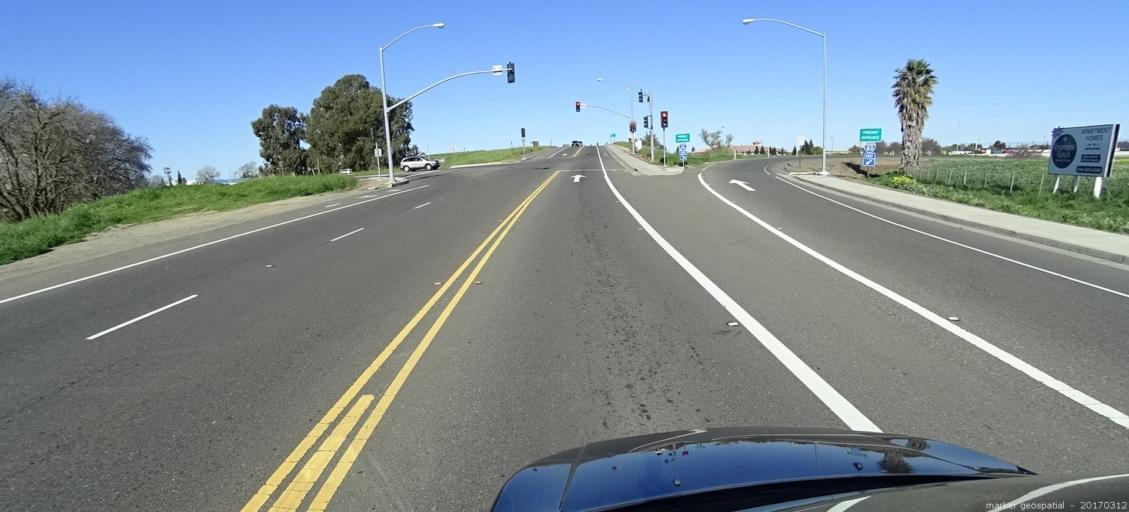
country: US
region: California
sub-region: Yolo County
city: West Sacramento
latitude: 38.6143
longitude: -121.5330
